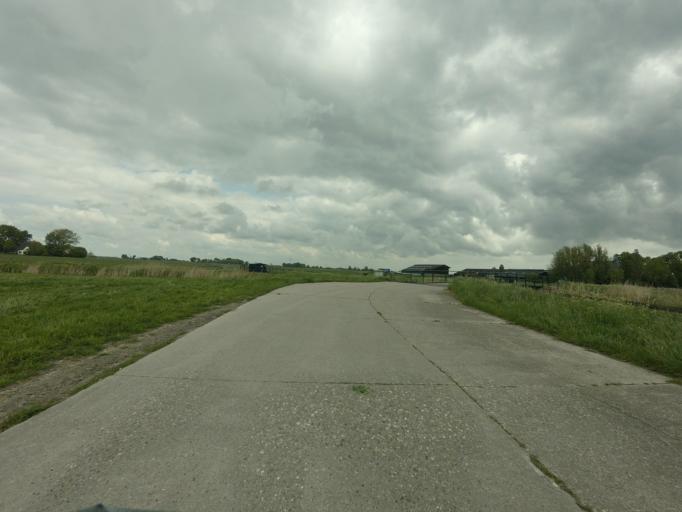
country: NL
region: Friesland
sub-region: Gemeente Littenseradiel
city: Wommels
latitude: 53.1070
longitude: 5.6210
